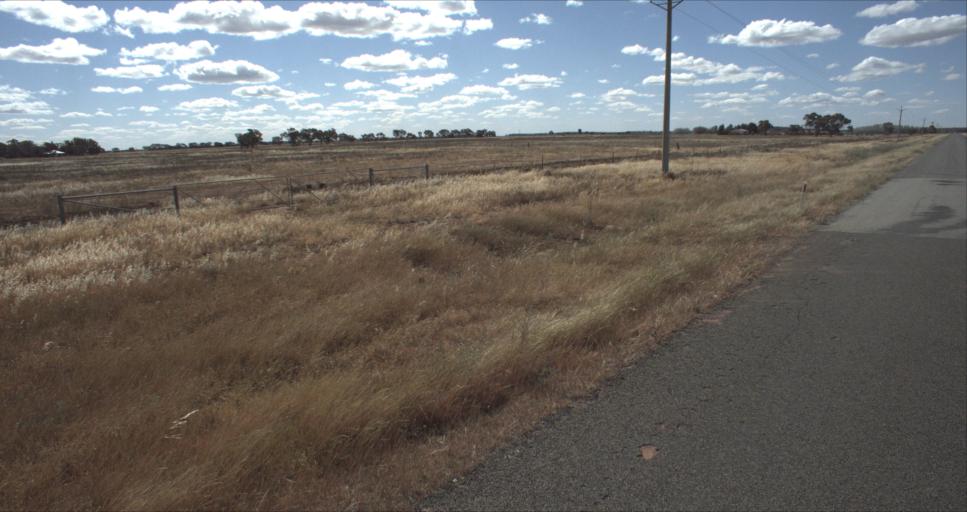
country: AU
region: New South Wales
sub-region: Leeton
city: Leeton
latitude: -34.4656
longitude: 146.2519
